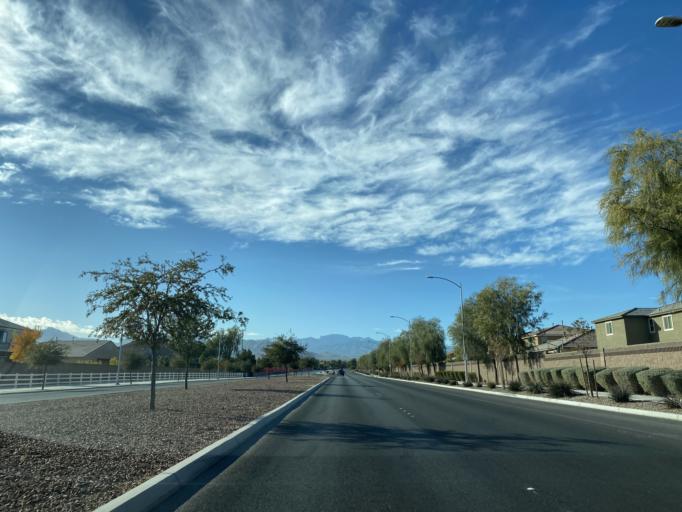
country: US
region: Nevada
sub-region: Clark County
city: North Las Vegas
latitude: 36.3052
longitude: -115.2537
